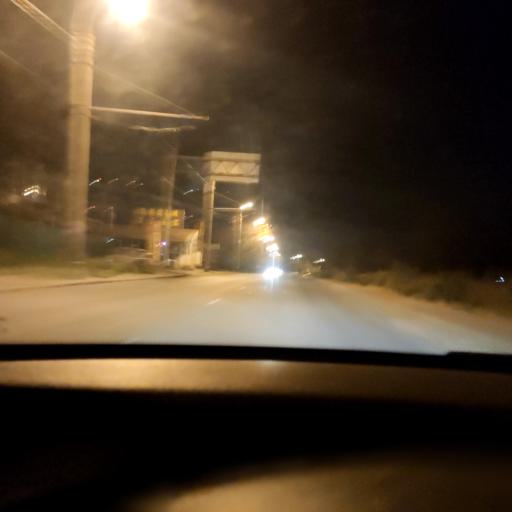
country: RU
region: Samara
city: Petra-Dubrava
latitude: 53.2541
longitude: 50.2665
